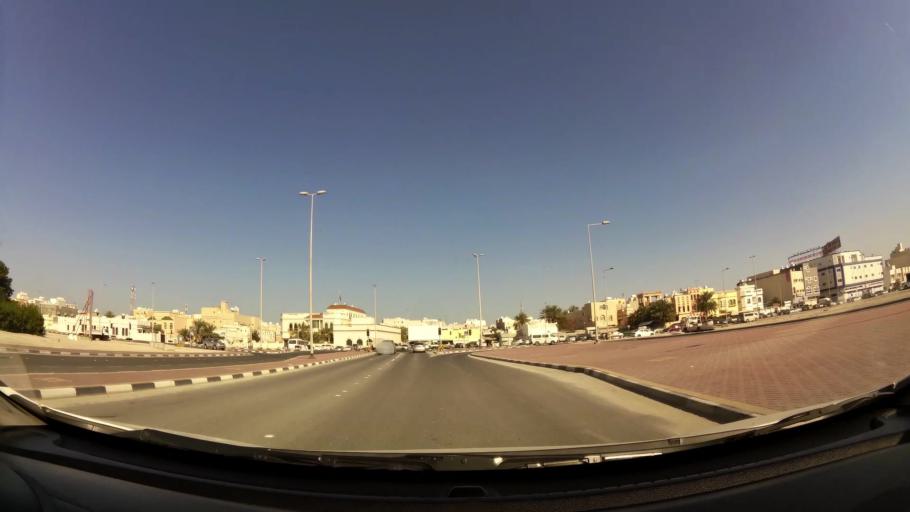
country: BH
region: Muharraq
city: Al Hadd
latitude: 26.2465
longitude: 50.6513
